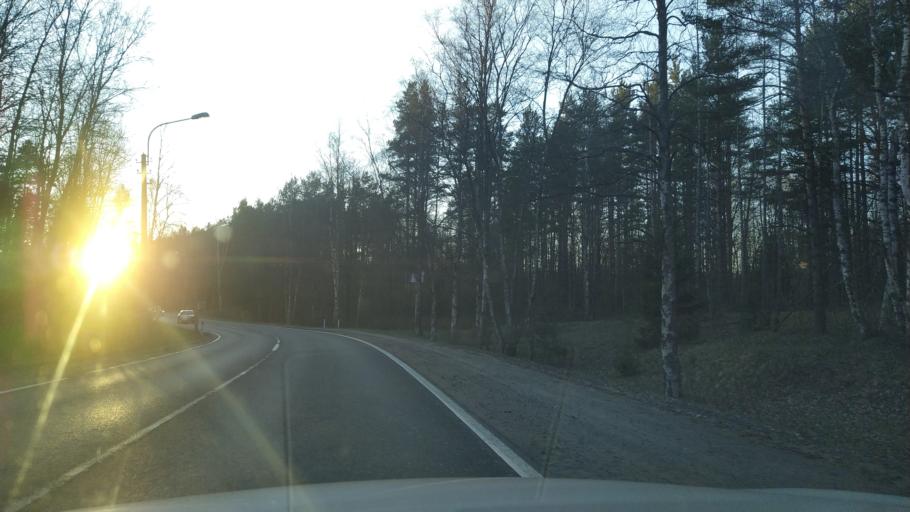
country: RU
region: St.-Petersburg
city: Beloostrov
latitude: 60.1381
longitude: 29.9778
